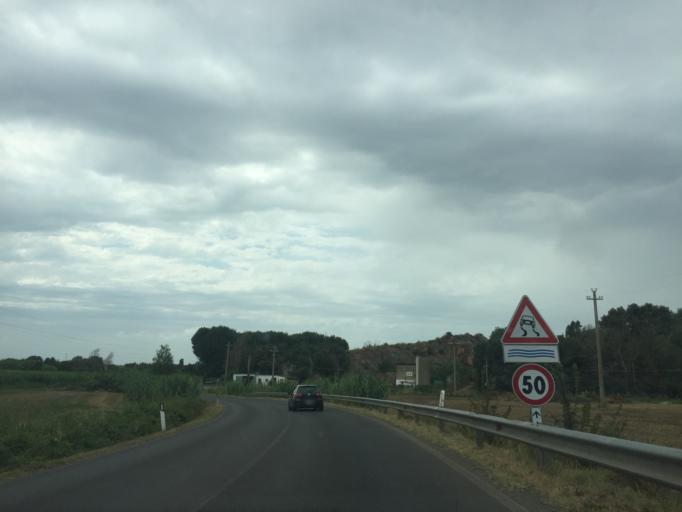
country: IT
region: Tuscany
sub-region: Province of Pisa
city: Asciano
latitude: 43.7353
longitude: 10.4764
